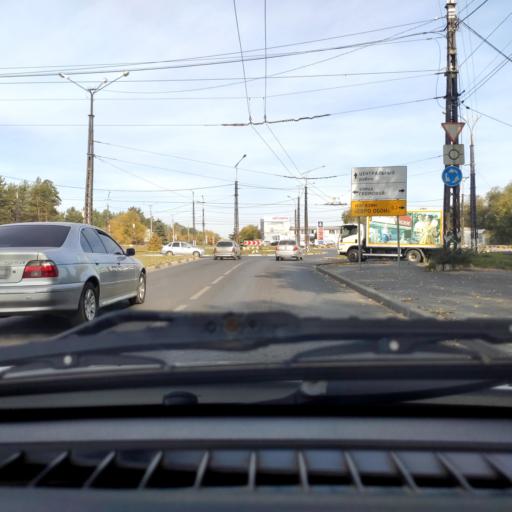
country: RU
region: Samara
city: Zhigulevsk
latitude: 53.4861
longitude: 49.4744
